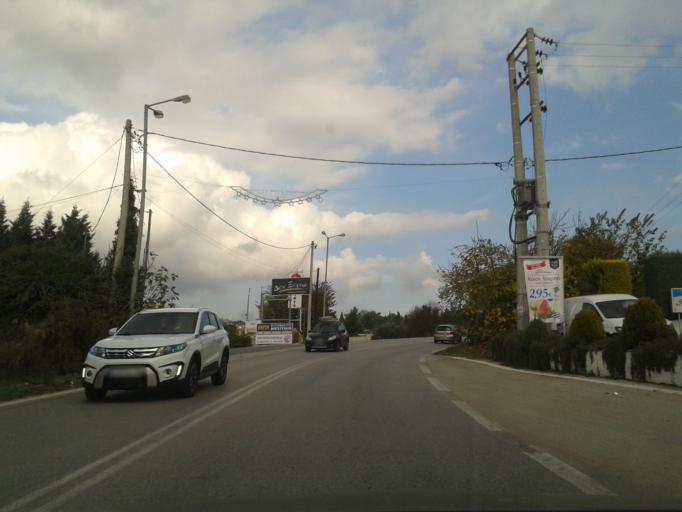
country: GR
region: Attica
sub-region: Nomarchia Anatolikis Attikis
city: Polydendri
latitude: 38.2085
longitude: 23.8698
